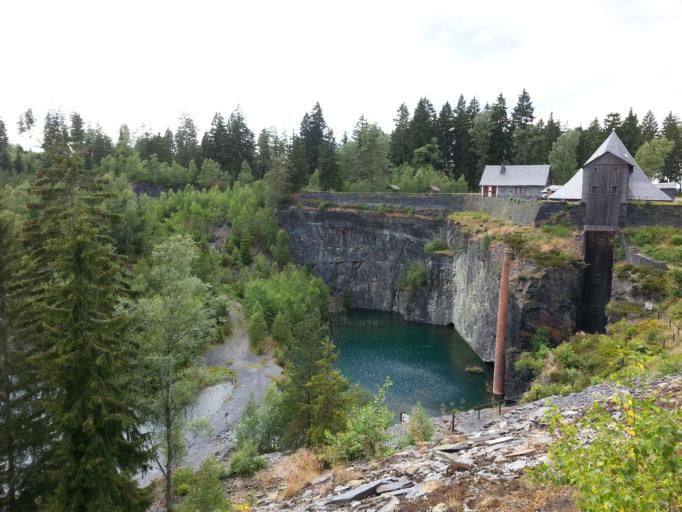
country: DE
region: Bavaria
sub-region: Upper Franconia
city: Reichenbach
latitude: 50.4605
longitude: 11.4329
